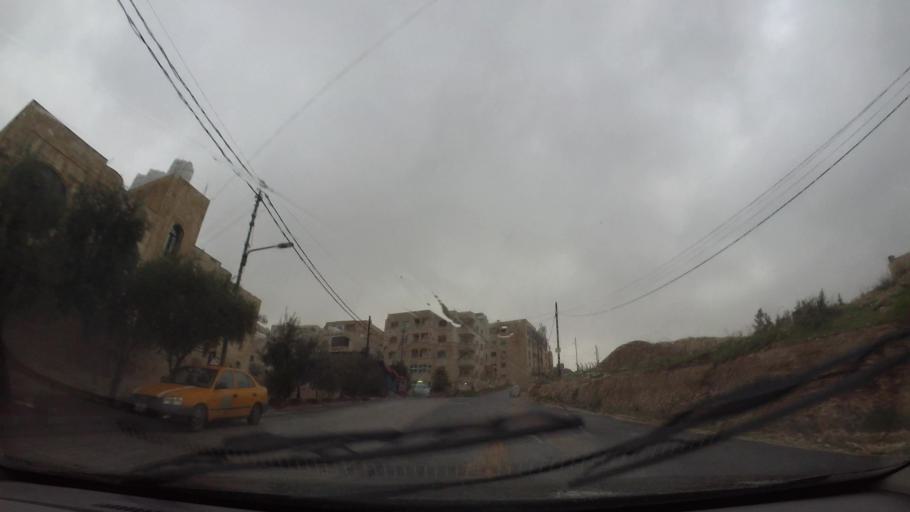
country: JO
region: Amman
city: Amman
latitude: 32.0055
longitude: 35.9330
